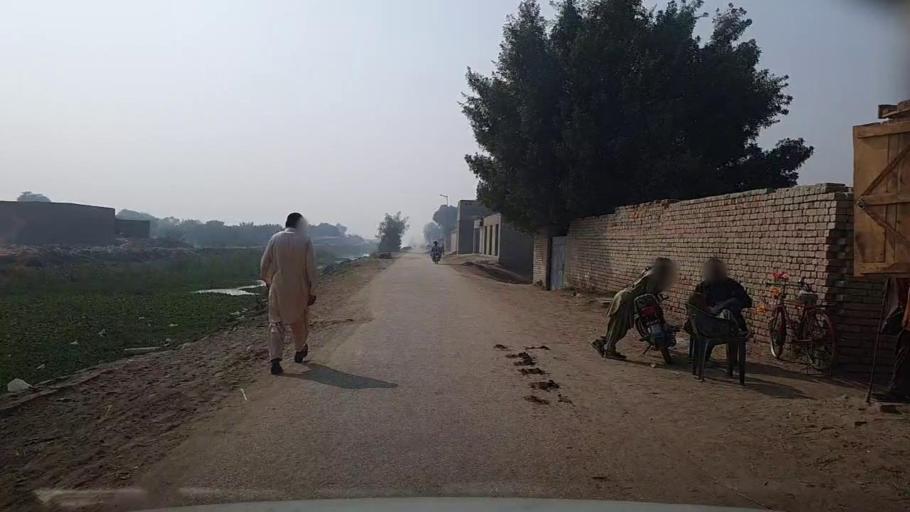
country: PK
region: Sindh
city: Setharja Old
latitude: 27.1994
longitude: 68.4826
